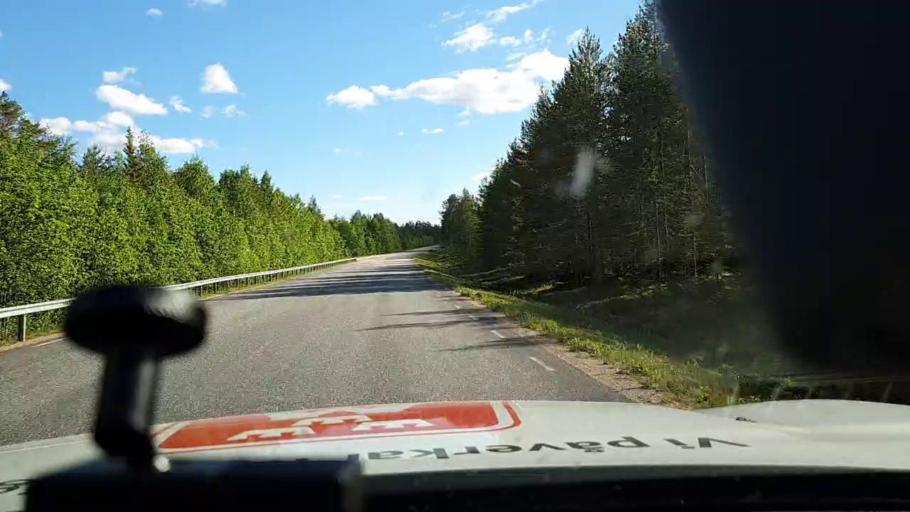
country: SE
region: Norrbotten
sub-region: Overtornea Kommun
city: OEvertornea
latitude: 66.3444
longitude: 23.6482
